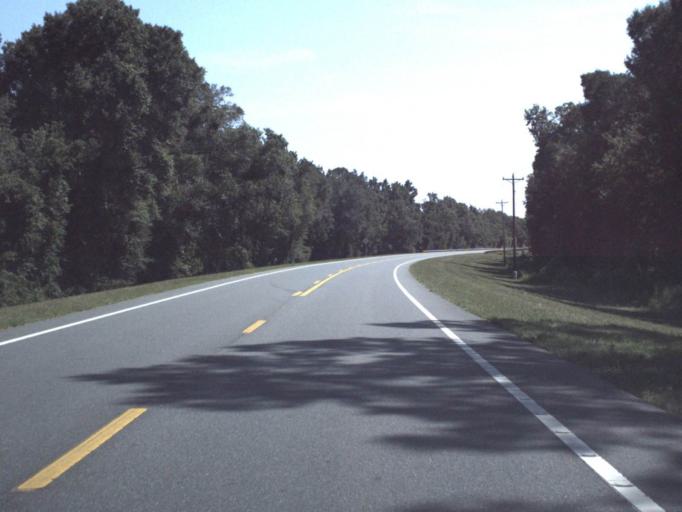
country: US
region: Florida
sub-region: Alachua County
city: Alachua
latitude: 29.8706
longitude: -82.3407
